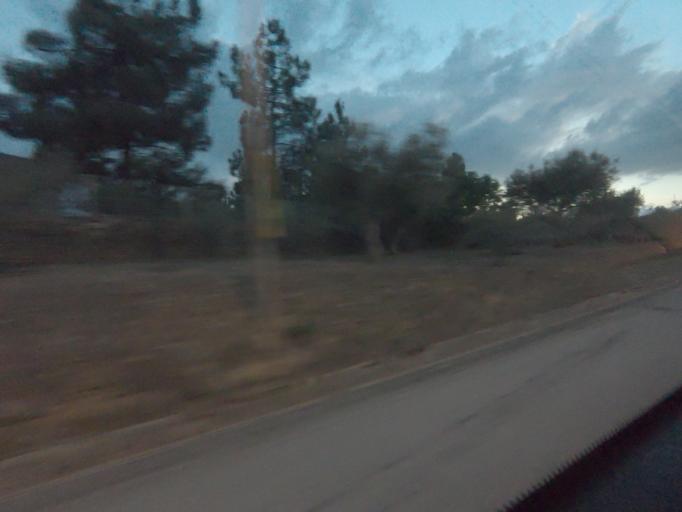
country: PT
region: Viseu
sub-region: Armamar
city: Armamar
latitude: 41.1066
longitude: -7.7092
